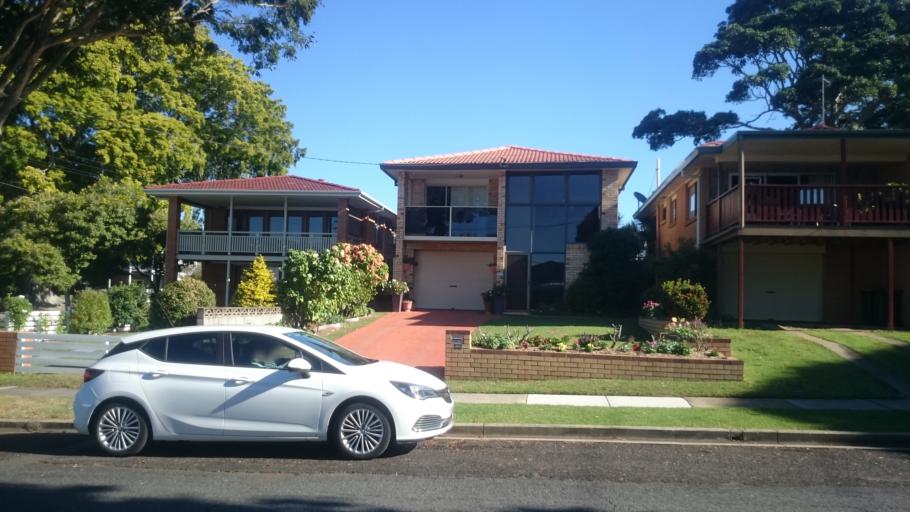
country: AU
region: Queensland
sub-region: Brisbane
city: Wynnum
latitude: -27.4515
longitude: 153.1838
